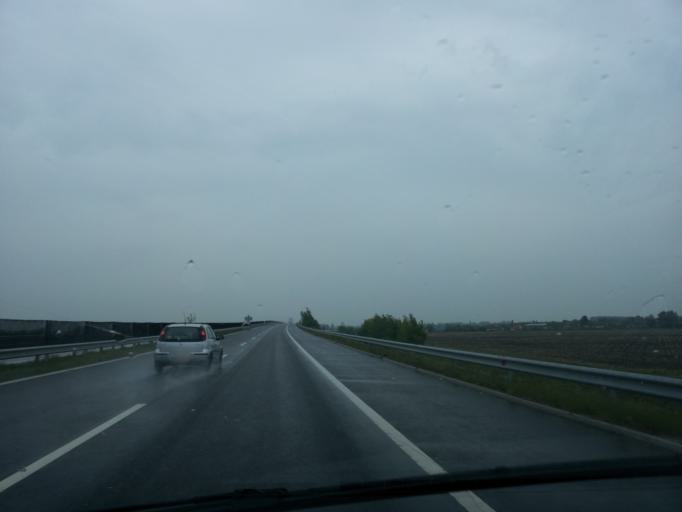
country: HU
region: Tolna
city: Ocseny
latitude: 46.3170
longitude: 18.7341
